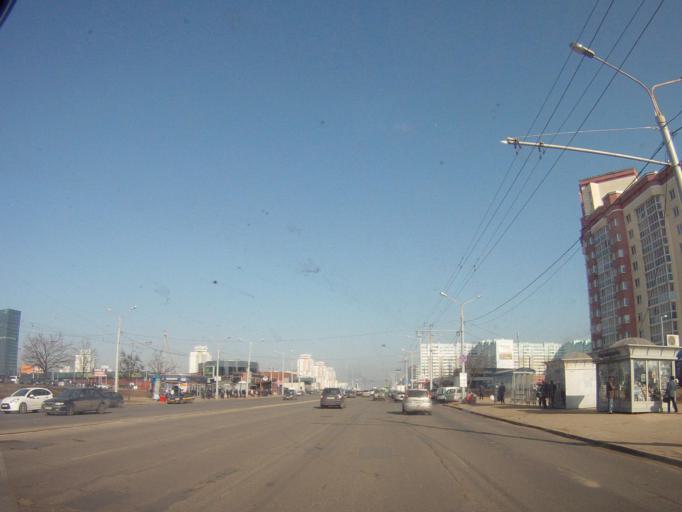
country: BY
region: Minsk
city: Novoye Medvezhino
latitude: 53.9053
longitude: 27.4358
